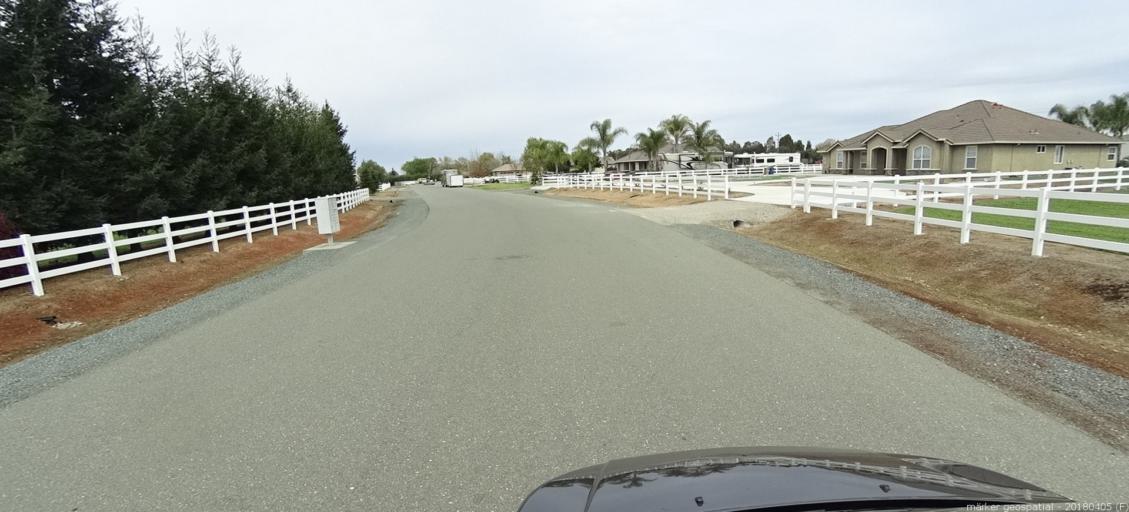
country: US
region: California
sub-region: Sacramento County
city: Galt
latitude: 38.2810
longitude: -121.3192
